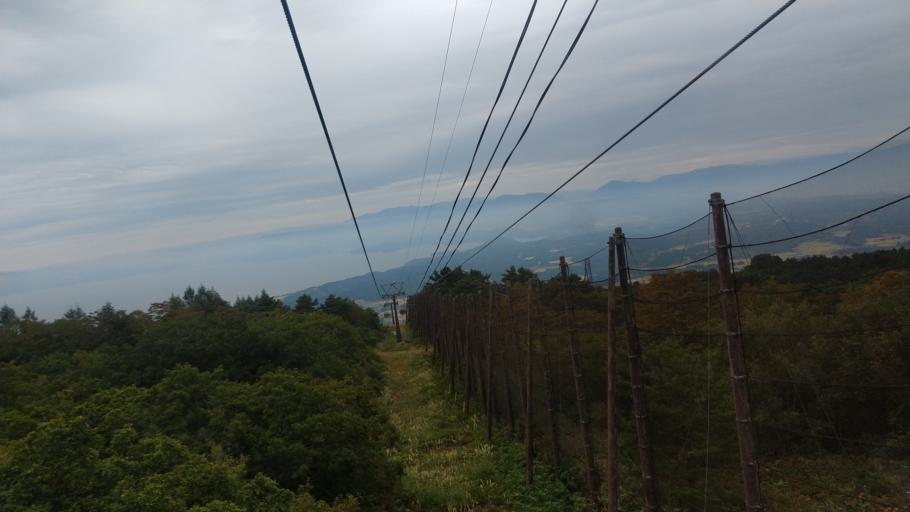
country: JP
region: Fukushima
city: Inawashiro
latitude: 37.5916
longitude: 140.0627
